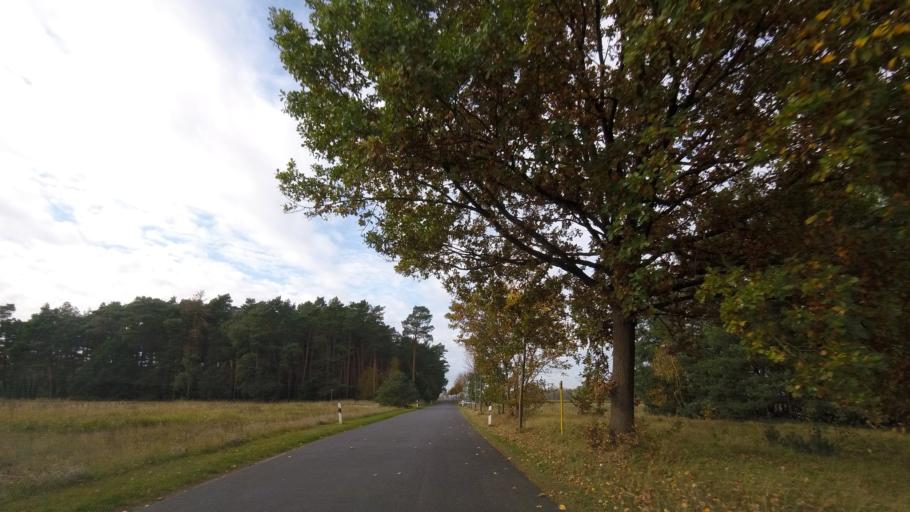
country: DE
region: Brandenburg
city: Beelitz
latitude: 52.1823
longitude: 12.9597
